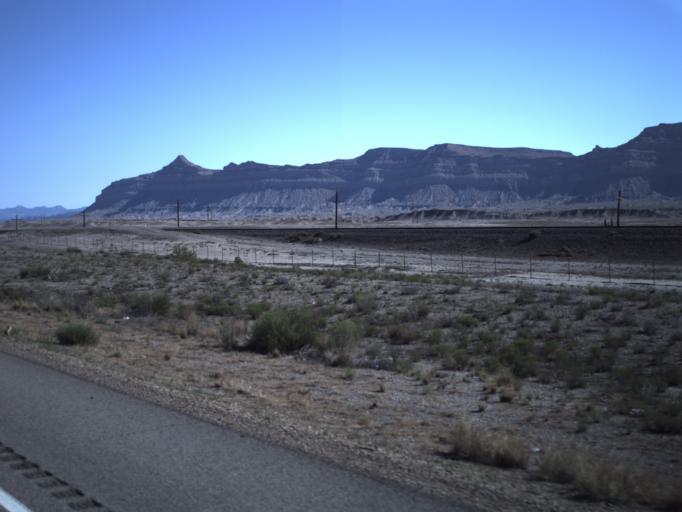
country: US
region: Utah
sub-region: Carbon County
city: East Carbon City
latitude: 39.1041
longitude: -110.3247
